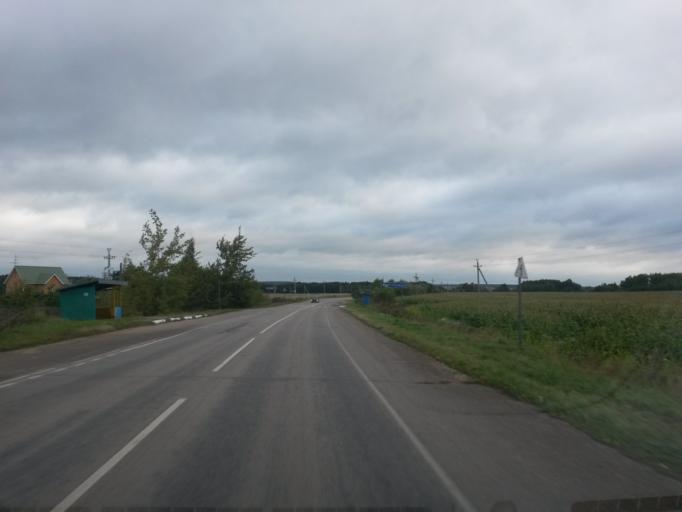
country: RU
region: Moskovskaya
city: Barybino
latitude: 55.2152
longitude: 37.7862
